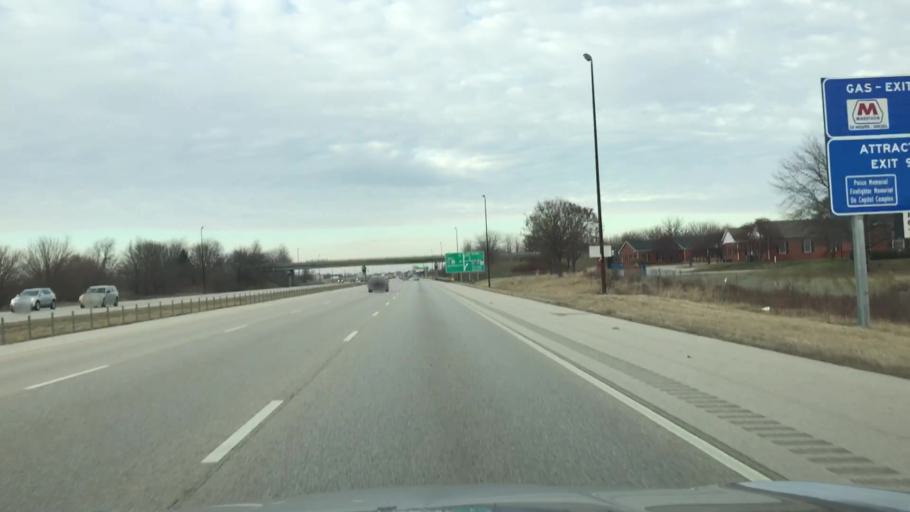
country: US
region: Illinois
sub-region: Sangamon County
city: Southern View
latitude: 39.7261
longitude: -89.6439
